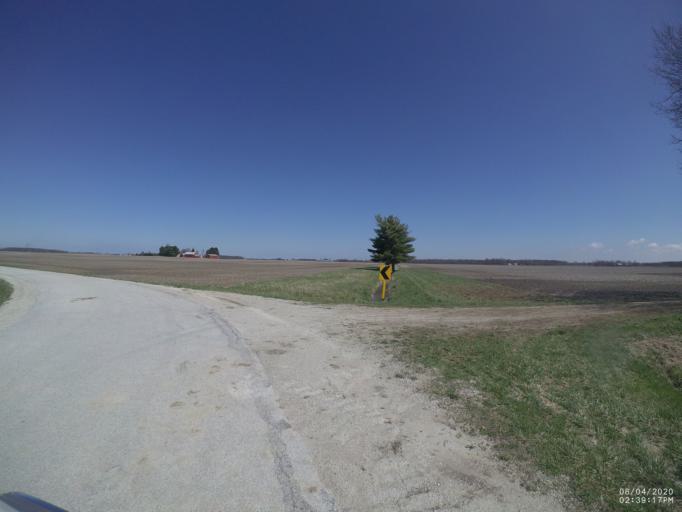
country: US
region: Ohio
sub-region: Sandusky County
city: Gibsonburg
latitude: 41.2800
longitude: -83.2933
